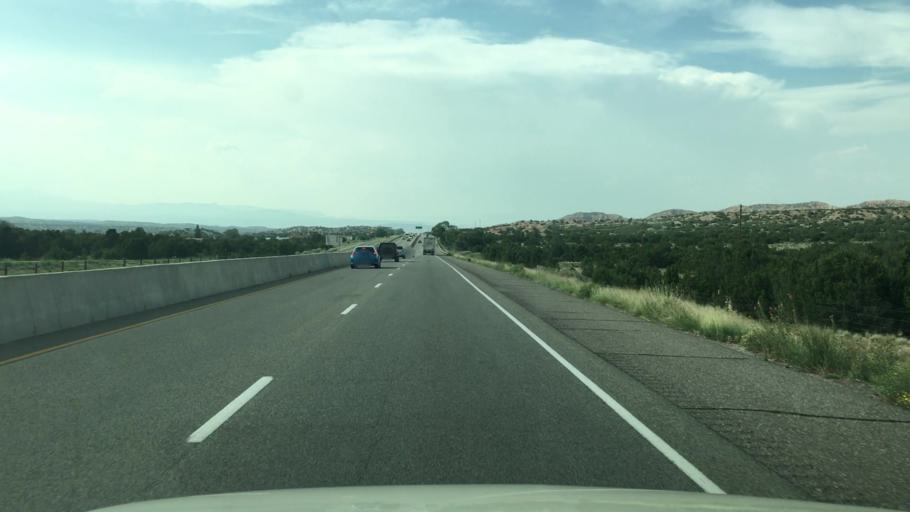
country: US
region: New Mexico
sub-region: Santa Fe County
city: Nambe
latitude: 35.7955
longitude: -105.9560
